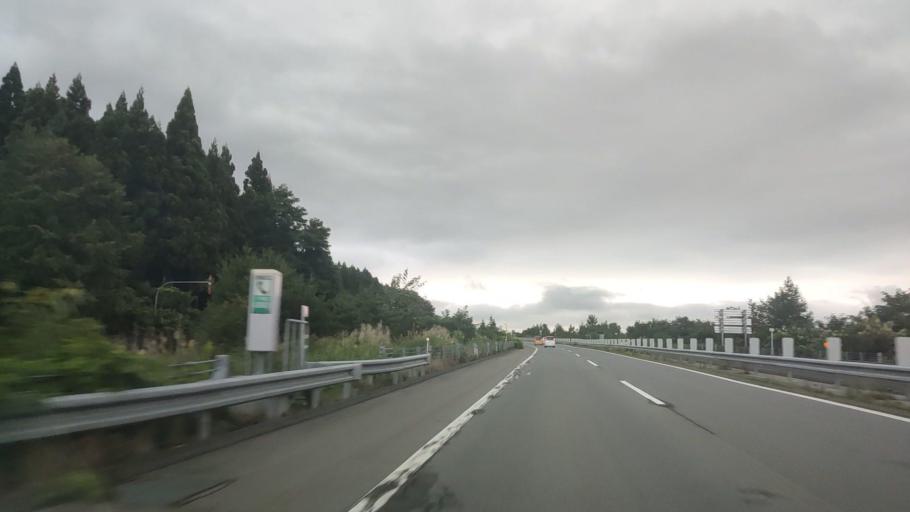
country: JP
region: Hokkaido
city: Nanae
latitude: 41.9055
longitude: 140.6975
